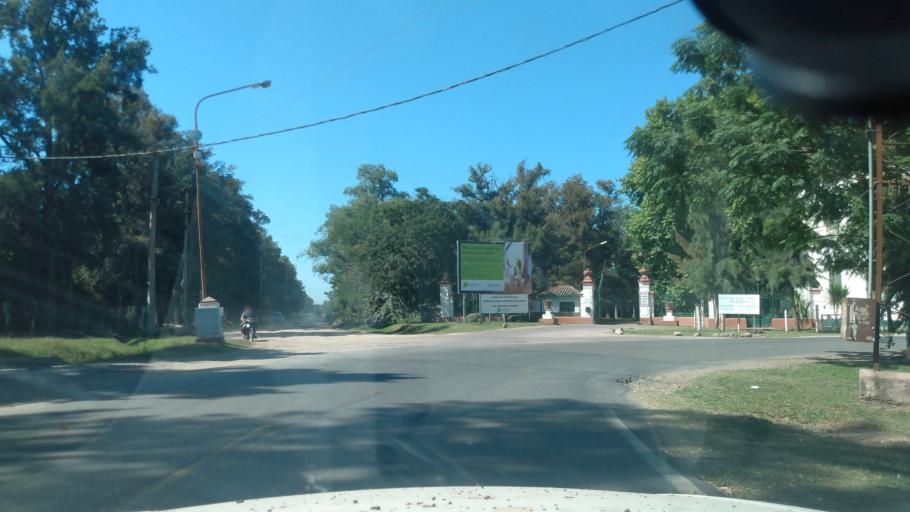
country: AR
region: Buenos Aires
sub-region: Partido de Lujan
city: Lujan
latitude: -34.5013
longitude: -59.0702
